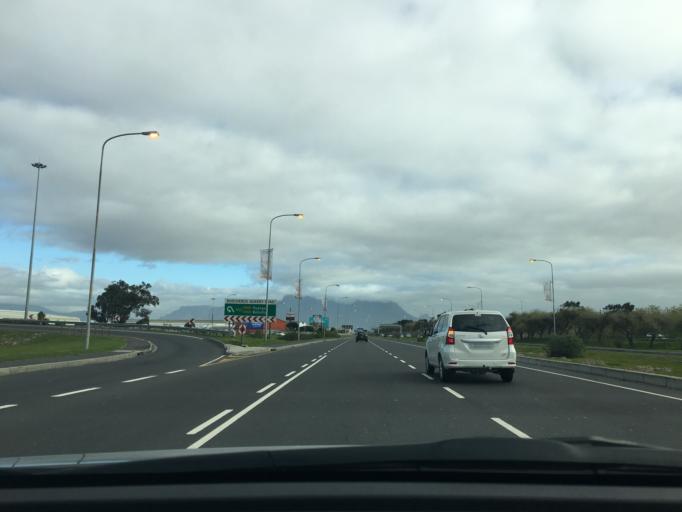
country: ZA
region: Western Cape
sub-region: City of Cape Town
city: Lansdowne
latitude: -33.9687
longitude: 18.5895
